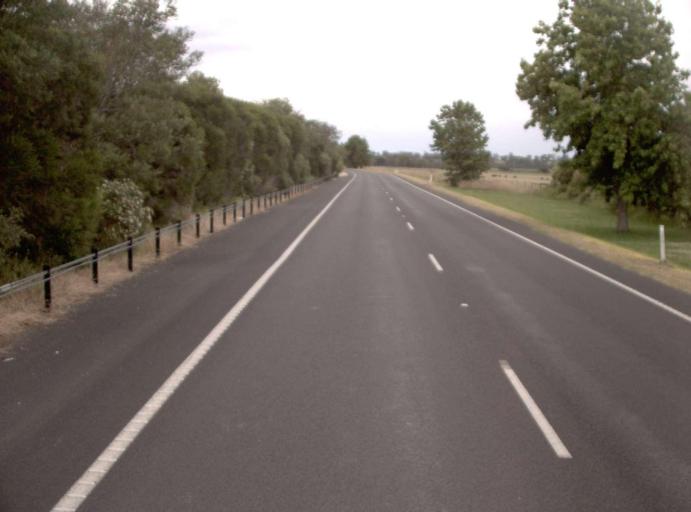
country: AU
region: Victoria
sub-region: East Gippsland
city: Bairnsdale
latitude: -37.8608
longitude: 147.6462
